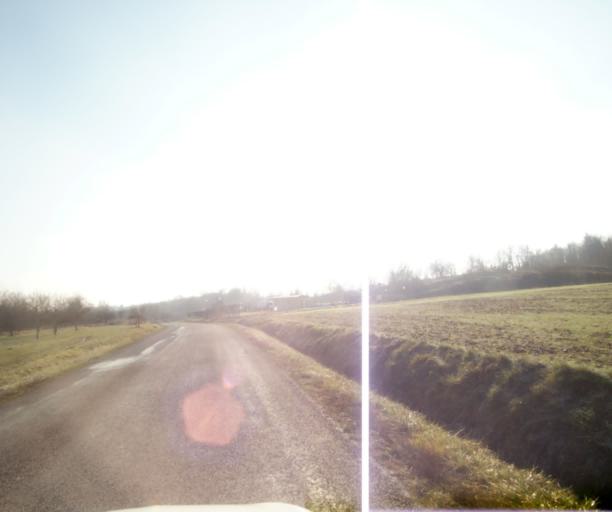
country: FR
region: Champagne-Ardenne
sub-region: Departement de la Haute-Marne
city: Wassy
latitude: 48.5015
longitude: 4.9284
